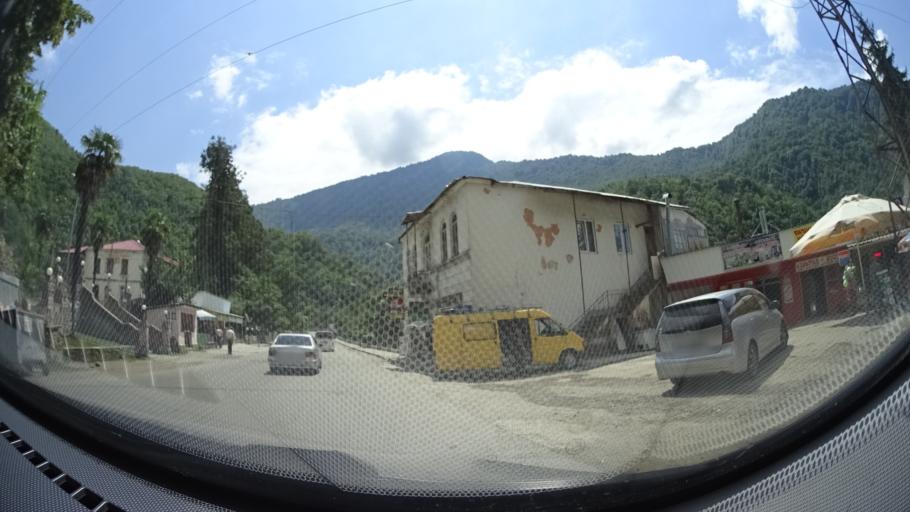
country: GE
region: Ajaria
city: Keda
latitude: 41.5725
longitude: 41.8580
